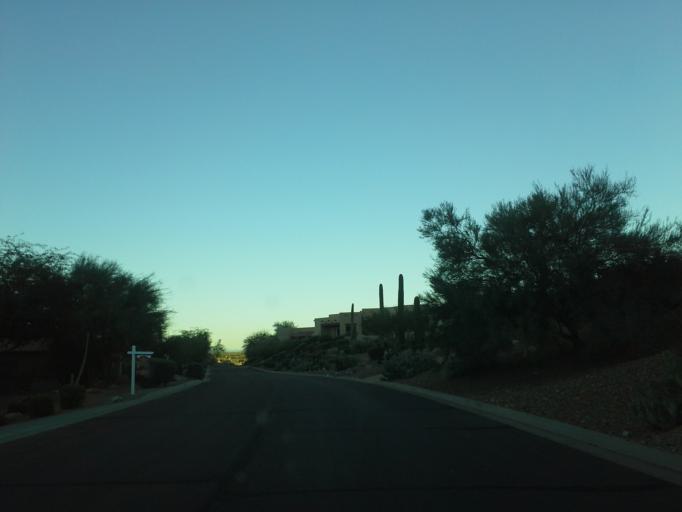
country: US
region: Arizona
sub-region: Pinal County
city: Apache Junction
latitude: 33.3717
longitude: -111.4408
